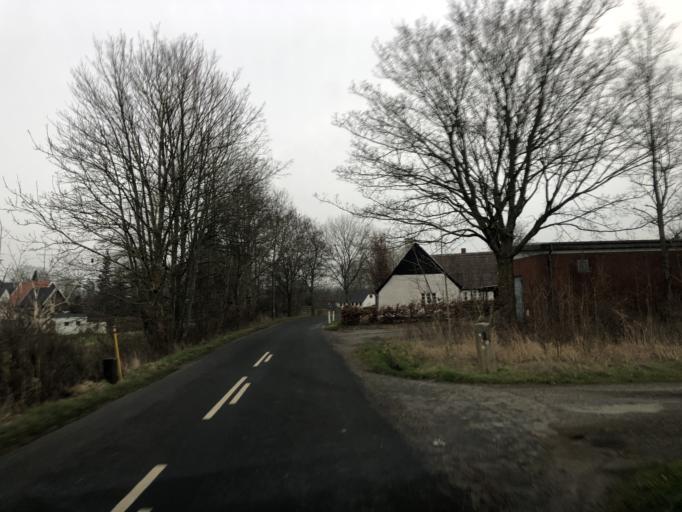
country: DK
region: South Denmark
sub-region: Faaborg-Midtfyn Kommune
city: Arslev
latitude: 55.3000
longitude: 10.4708
